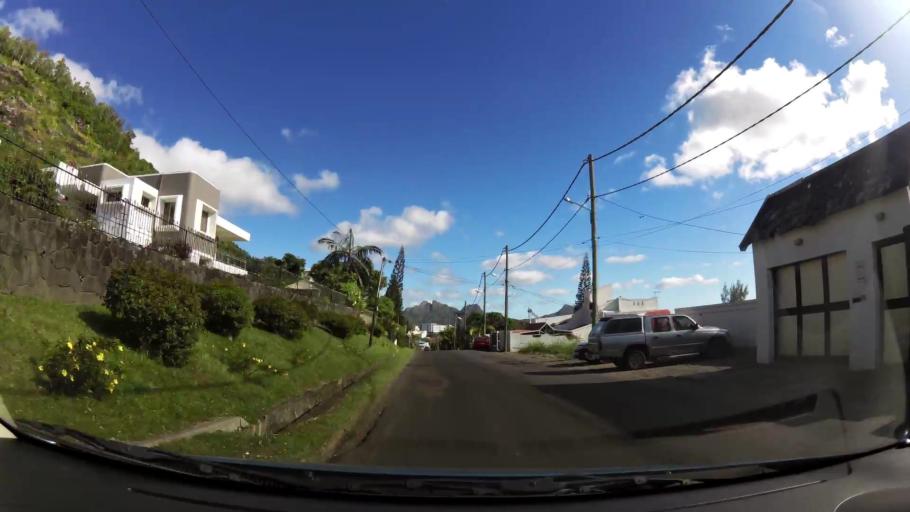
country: MU
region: Plaines Wilhems
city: Quatre Bornes
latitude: -20.2735
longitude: 57.4814
